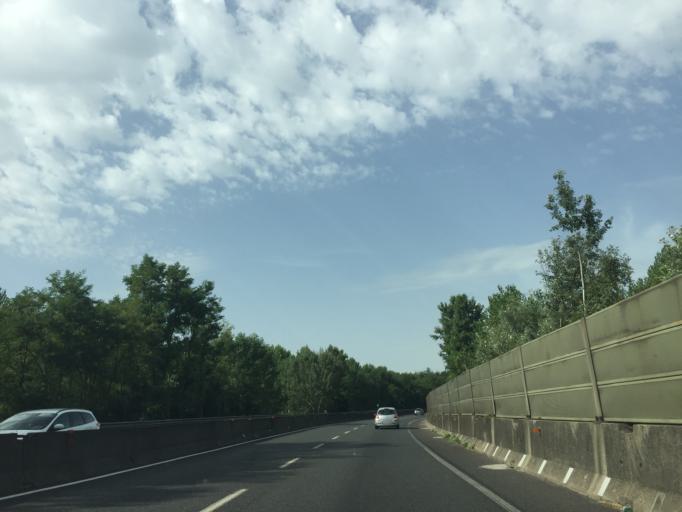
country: IT
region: Tuscany
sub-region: Province of Pisa
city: La Rotta
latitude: 43.6657
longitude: 10.7101
